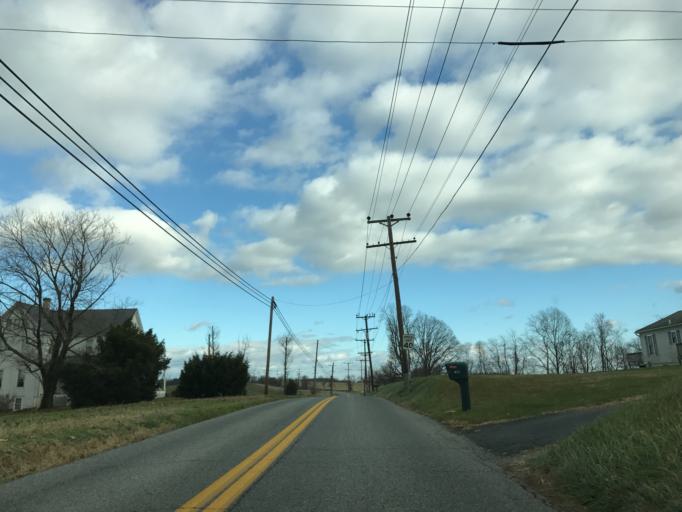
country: US
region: Pennsylvania
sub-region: York County
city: Stewartstown
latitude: 39.6359
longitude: -76.5927
